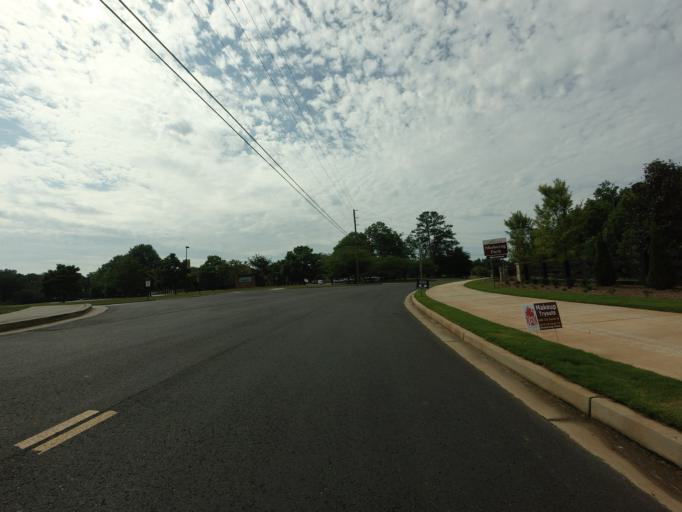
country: US
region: Georgia
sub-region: Gwinnett County
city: Duluth
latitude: 34.0470
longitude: -84.1305
